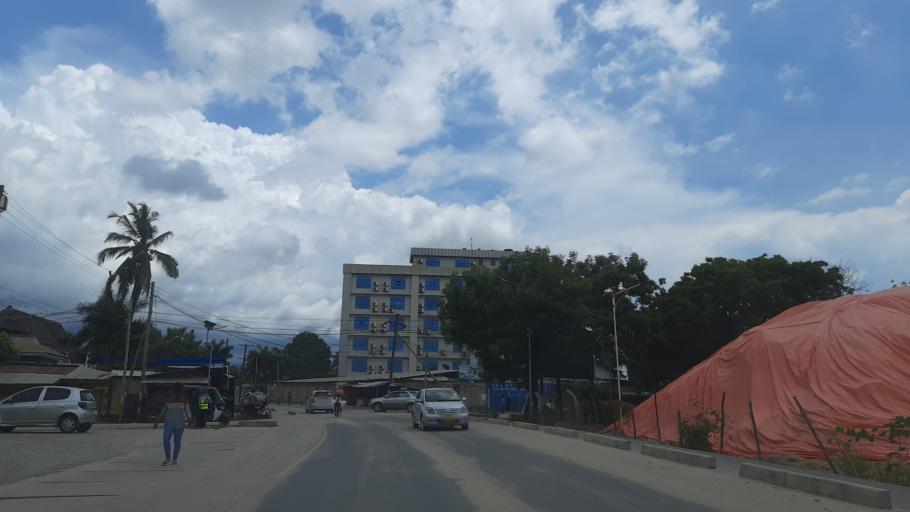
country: TZ
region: Dar es Salaam
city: Magomeni
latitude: -6.7697
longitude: 39.2280
